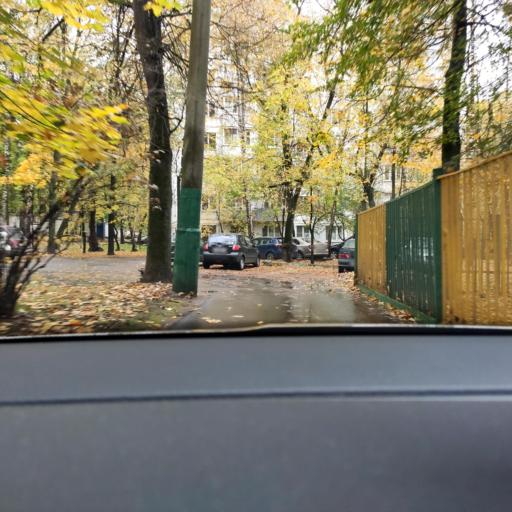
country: RU
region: Moscow
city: Rostokino
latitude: 55.8281
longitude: 37.6646
